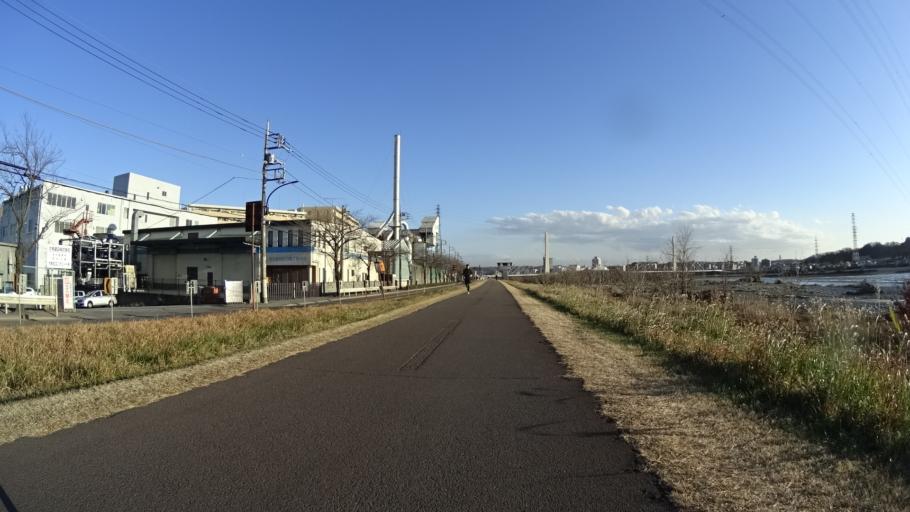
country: JP
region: Tokyo
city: Hino
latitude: 35.6654
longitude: 139.4364
